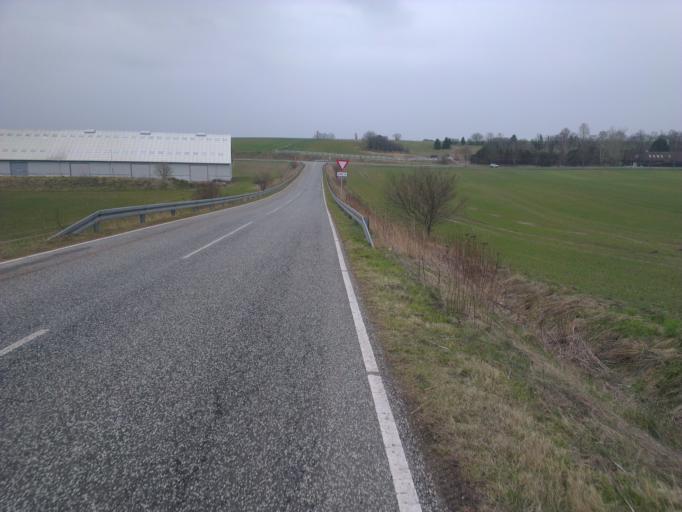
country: DK
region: Capital Region
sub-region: Frederikssund Kommune
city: Slangerup
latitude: 55.8321
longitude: 12.1819
